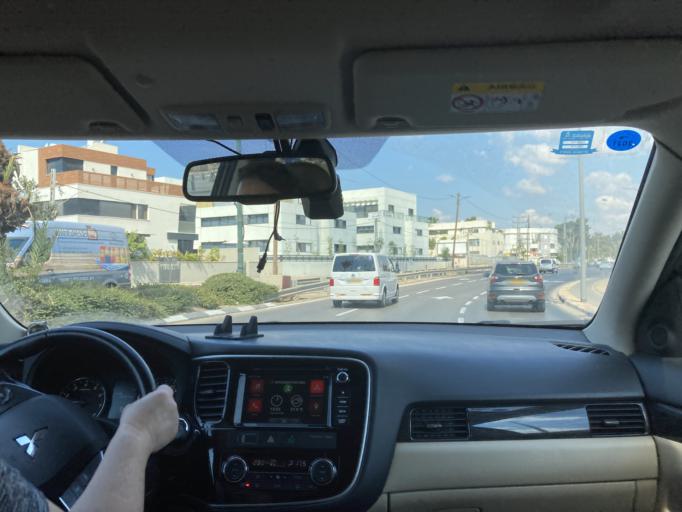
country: IL
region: Tel Aviv
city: Ramat HaSharon
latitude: 32.1227
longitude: 34.8241
